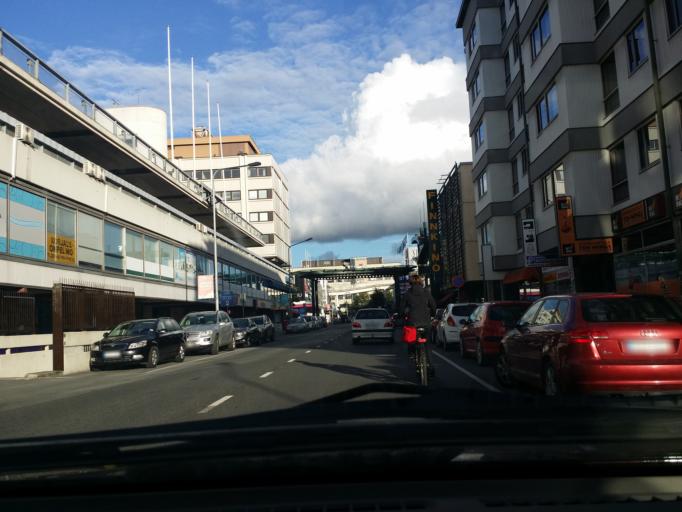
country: FI
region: Satakunta
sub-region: Pori
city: Pori
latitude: 61.4841
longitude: 21.7947
